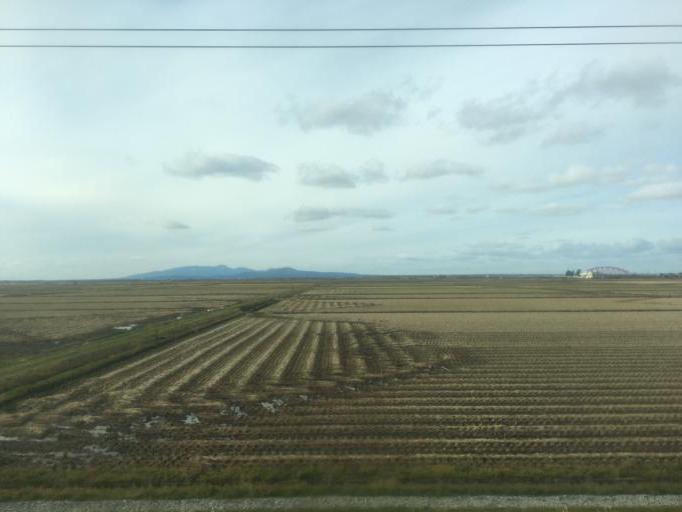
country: JP
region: Akita
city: Tenno
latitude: 39.9317
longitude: 140.0787
